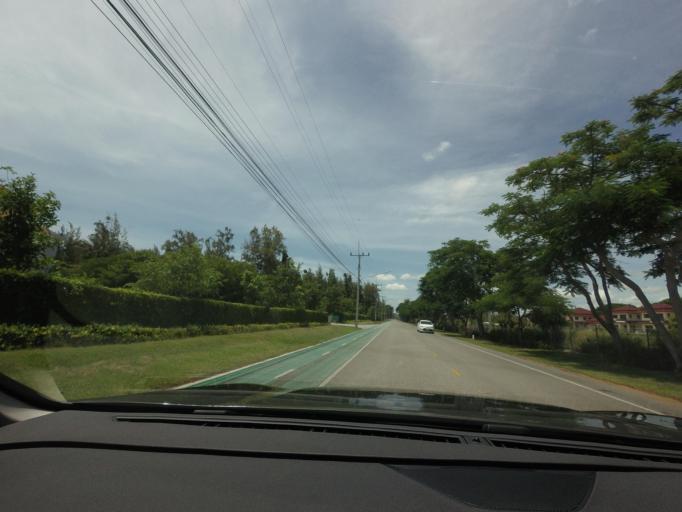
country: TH
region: Prachuap Khiri Khan
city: Hua Hin
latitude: 12.5027
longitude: 99.9727
